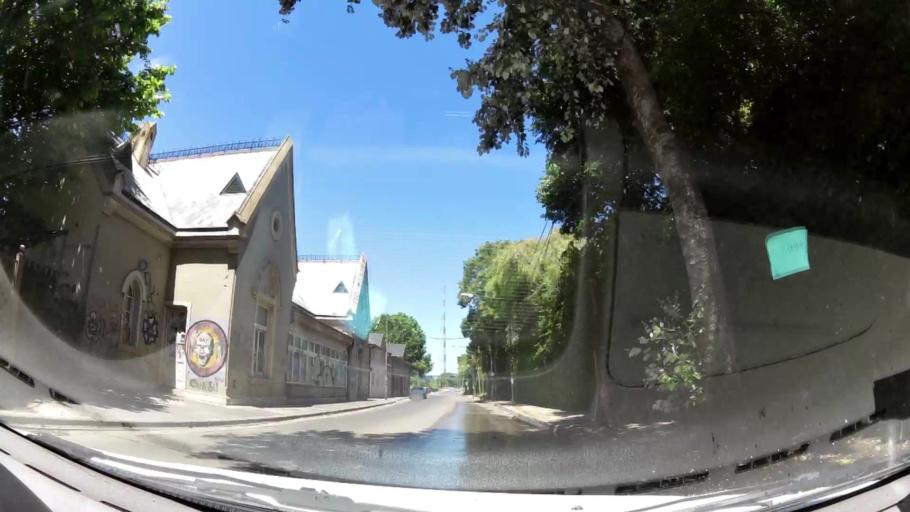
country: AR
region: Buenos Aires
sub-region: Partido de Vicente Lopez
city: Olivos
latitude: -34.4889
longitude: -58.4814
